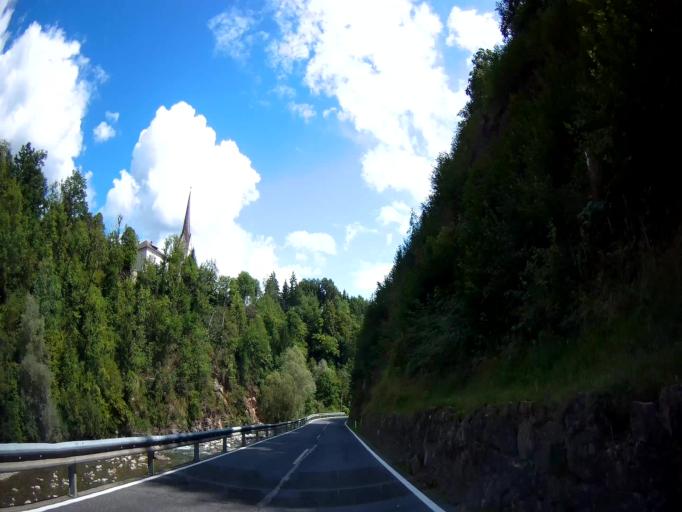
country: AT
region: Carinthia
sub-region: Politischer Bezirk Spittal an der Drau
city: Seeboden
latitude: 46.8325
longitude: 13.4910
